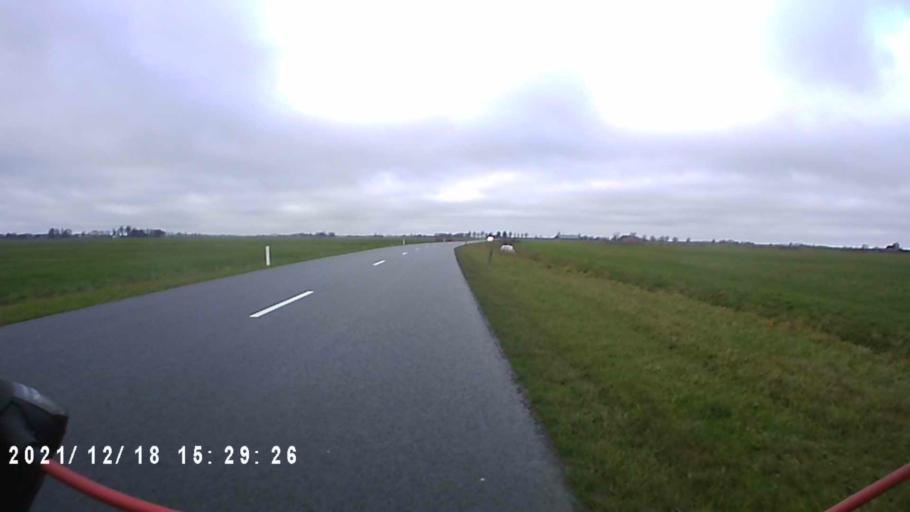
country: NL
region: Friesland
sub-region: Gemeente Dongeradeel
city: Anjum
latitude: 53.3343
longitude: 6.1415
